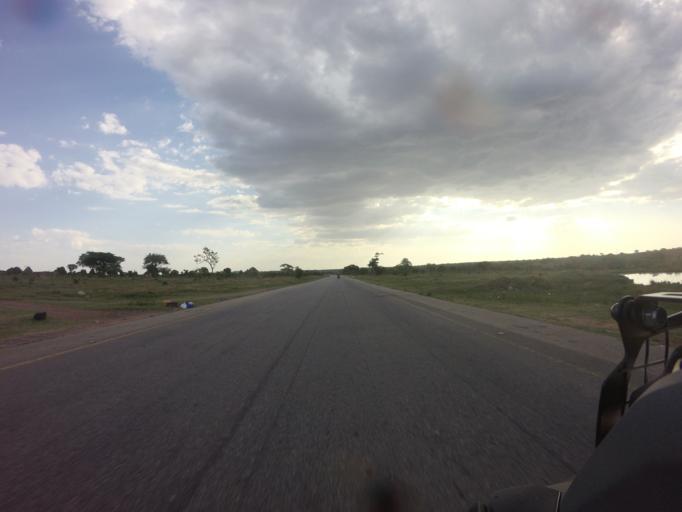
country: AO
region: Huila
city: Lubango
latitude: -14.5488
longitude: 14.0783
